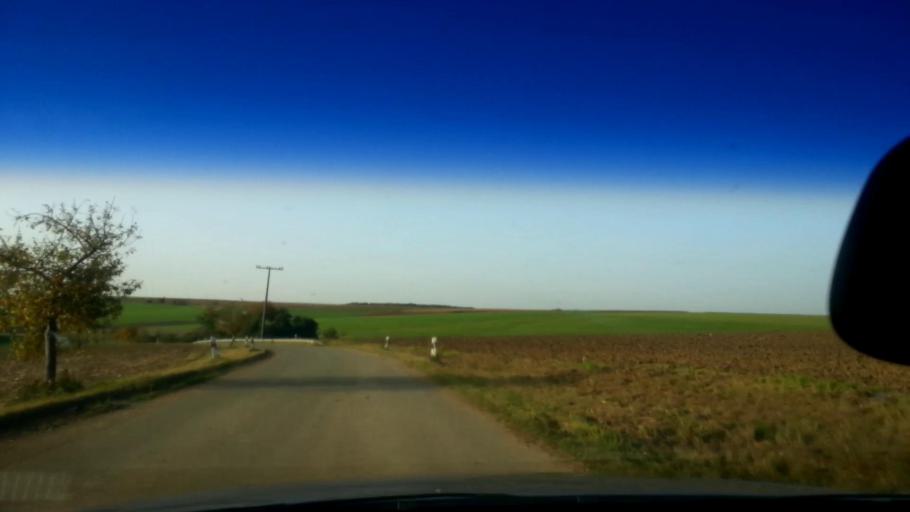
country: DE
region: Bavaria
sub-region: Upper Franconia
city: Ebensfeld
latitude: 50.0240
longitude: 10.9933
